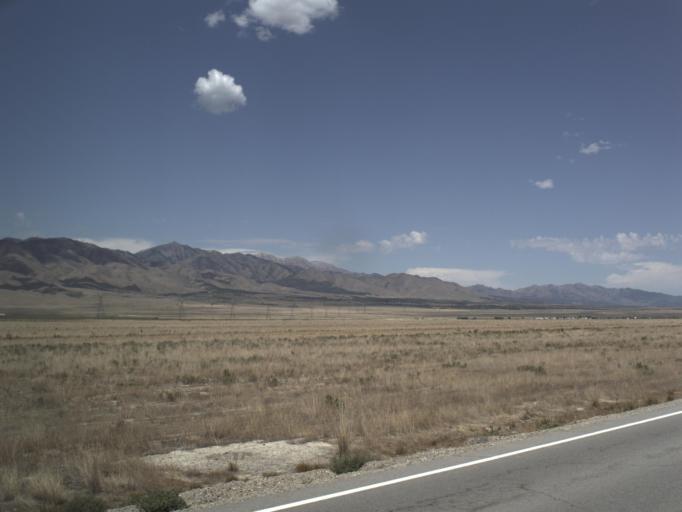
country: US
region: Utah
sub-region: Tooele County
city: Tooele
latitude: 40.3508
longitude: -112.4122
